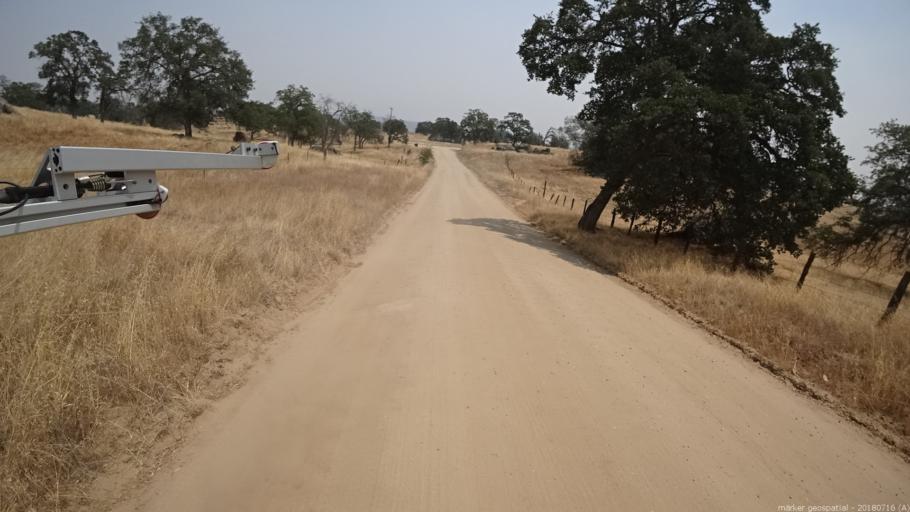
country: US
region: California
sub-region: Madera County
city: Yosemite Lakes
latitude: 37.2028
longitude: -119.9105
